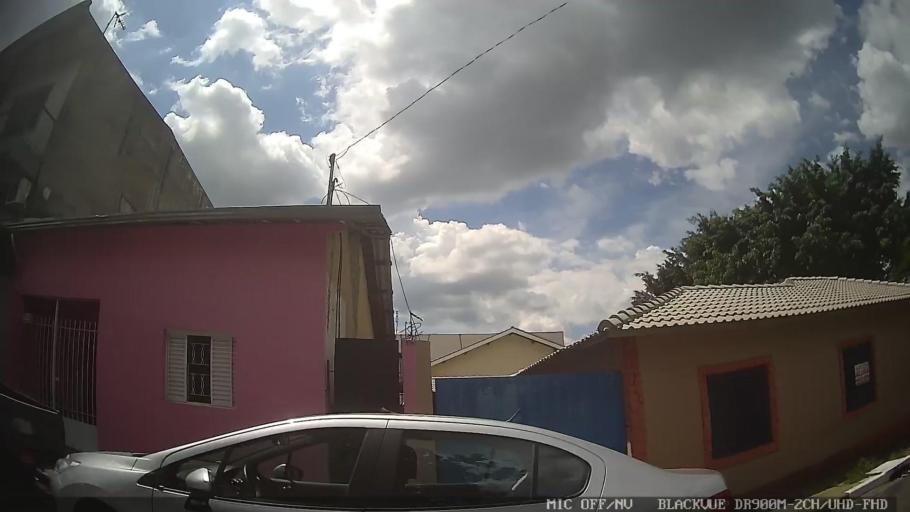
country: BR
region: Sao Paulo
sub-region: Atibaia
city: Atibaia
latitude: -23.1191
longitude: -46.5608
